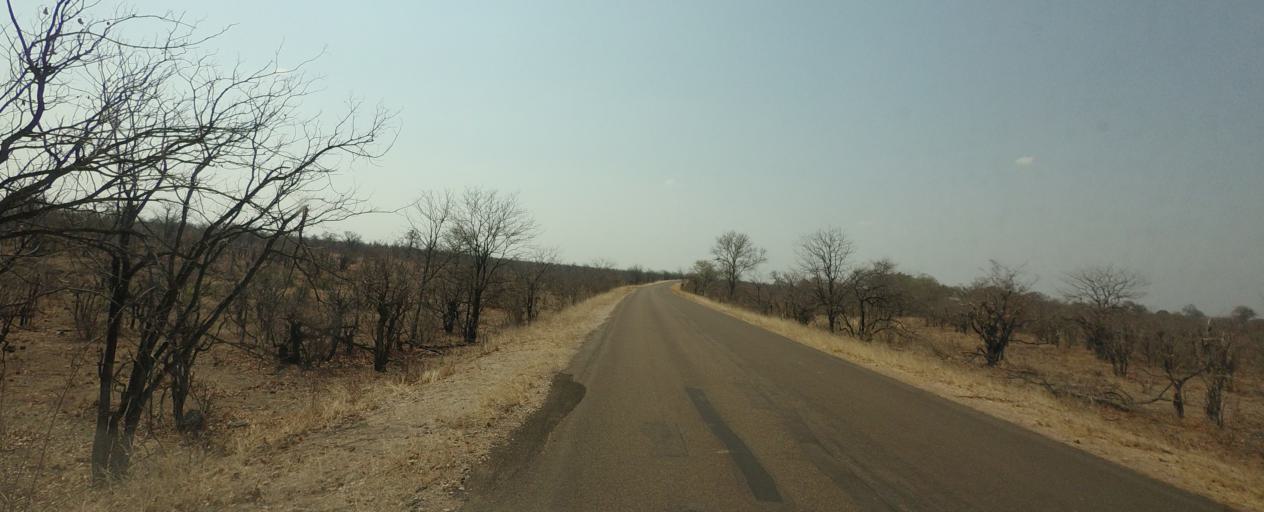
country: ZA
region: Limpopo
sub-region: Mopani District Municipality
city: Giyani
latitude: -23.2392
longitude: 31.3143
